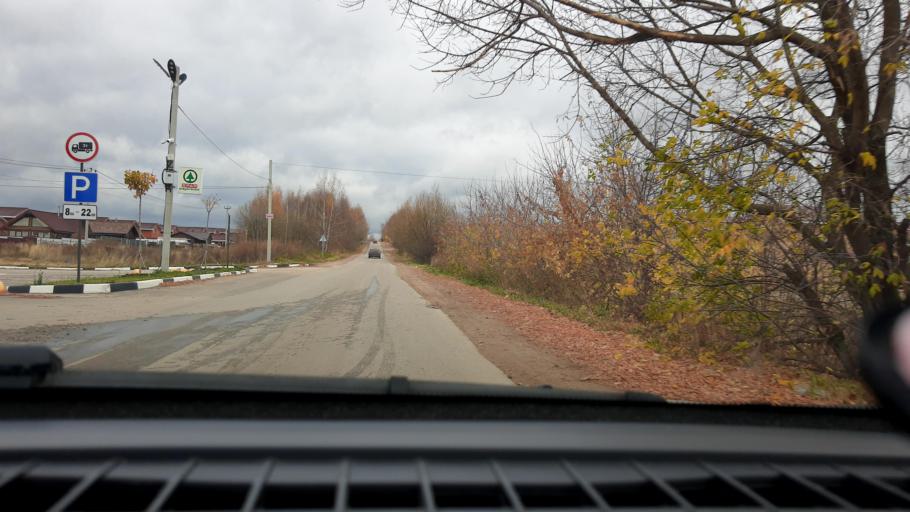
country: RU
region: Nizjnij Novgorod
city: Afonino
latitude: 56.2014
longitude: 44.1342
